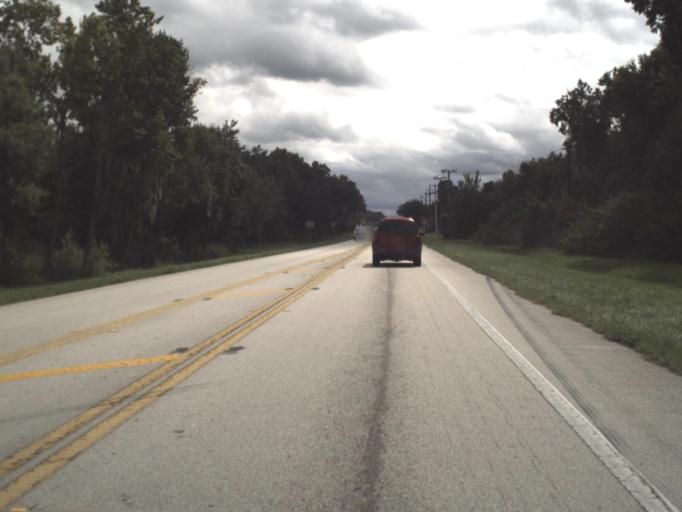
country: US
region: Florida
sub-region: Manatee County
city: Ellenton
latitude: 27.5922
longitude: -82.4255
